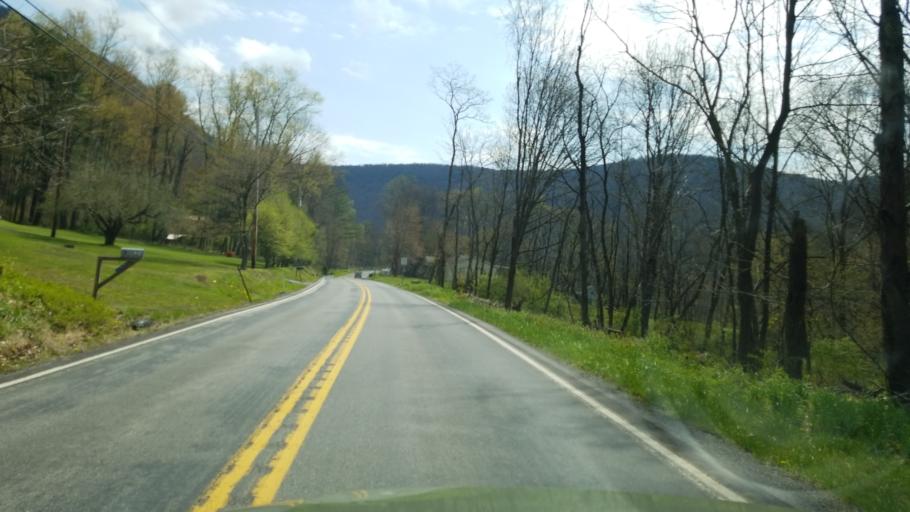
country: US
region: Pennsylvania
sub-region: Clinton County
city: Renovo
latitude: 41.2784
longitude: -77.8664
